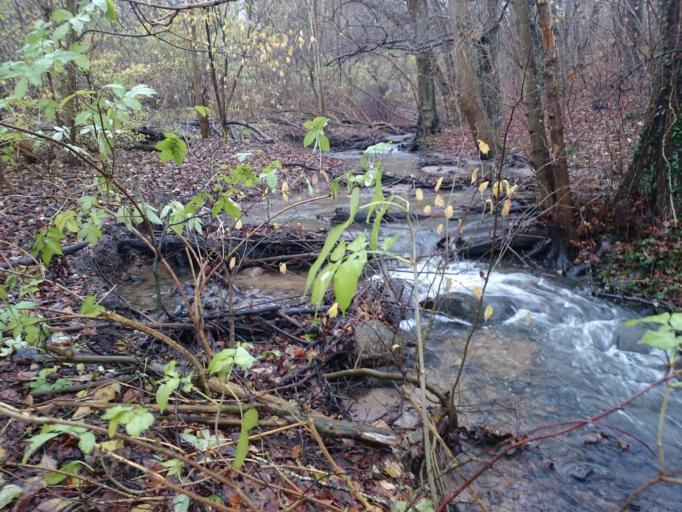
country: DK
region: Central Jutland
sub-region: Arhus Kommune
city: Stavtrup
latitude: 56.1273
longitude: 10.1320
